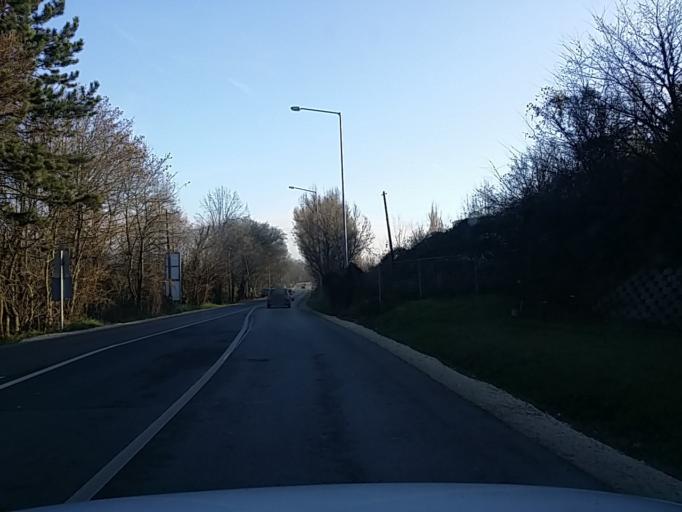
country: HU
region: Pest
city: Solymar
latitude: 47.5585
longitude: 18.9219
